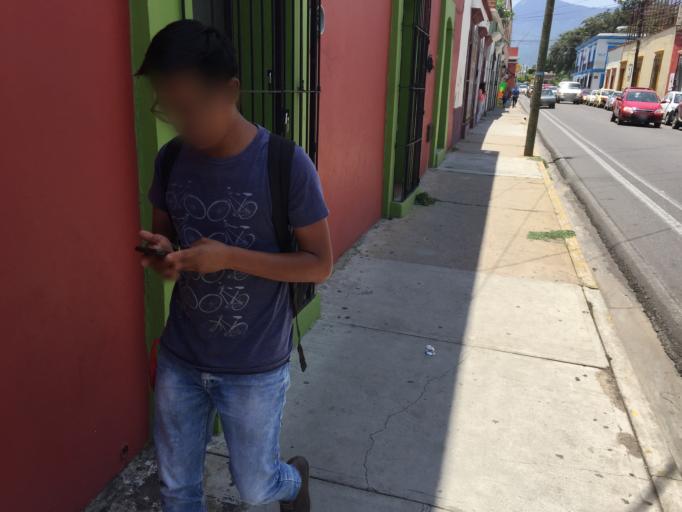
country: MX
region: Oaxaca
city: Oaxaca de Juarez
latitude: 17.0593
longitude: -96.7201
